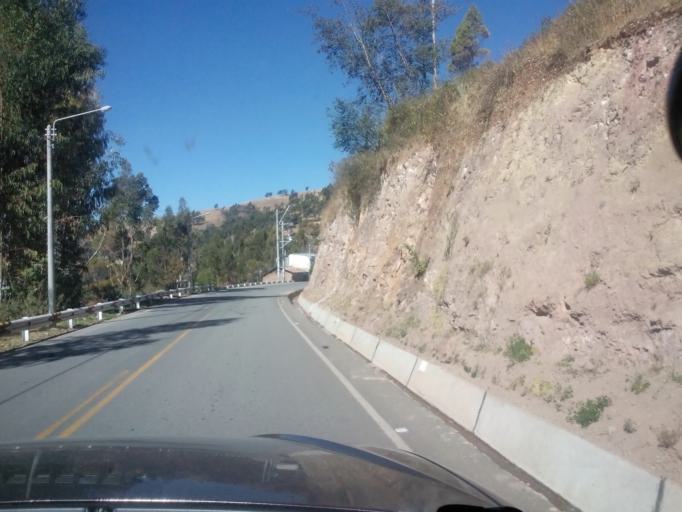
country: PE
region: Apurimac
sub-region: Provincia de Andahuaylas
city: Talavera
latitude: -13.6560
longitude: -73.4978
